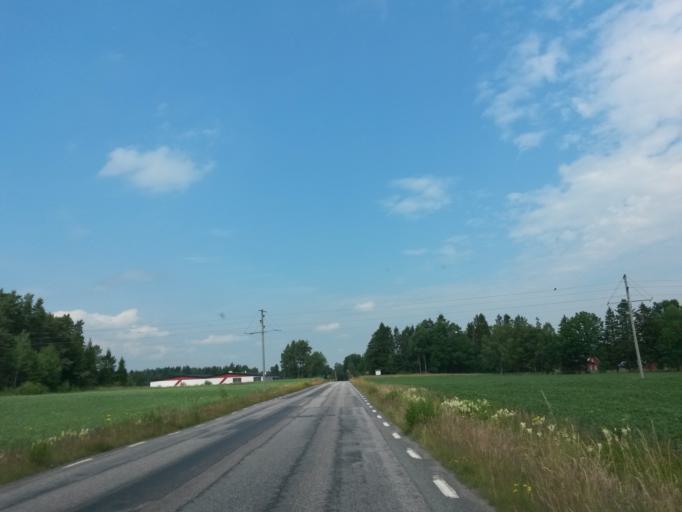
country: SE
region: Vaestra Goetaland
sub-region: Essunga Kommun
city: Nossebro
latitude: 58.1807
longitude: 12.7344
